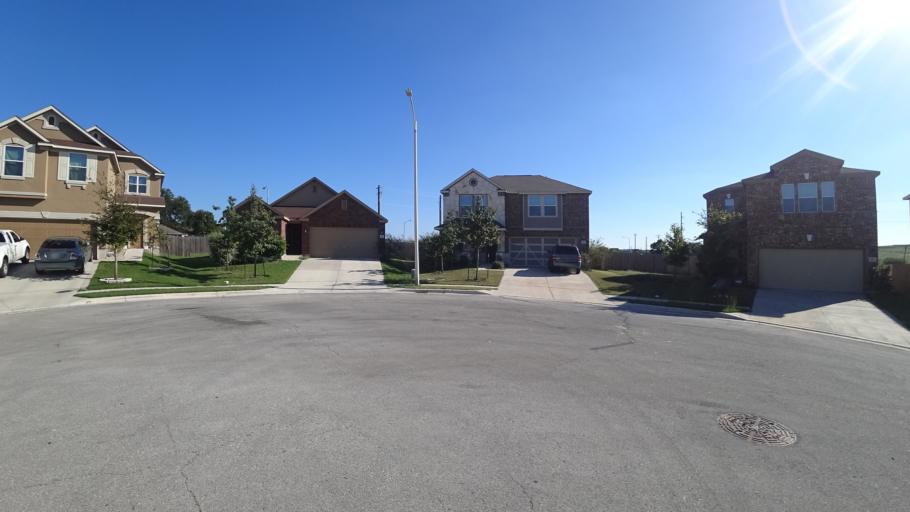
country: US
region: Texas
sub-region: Travis County
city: Manor
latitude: 30.3450
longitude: -97.6156
